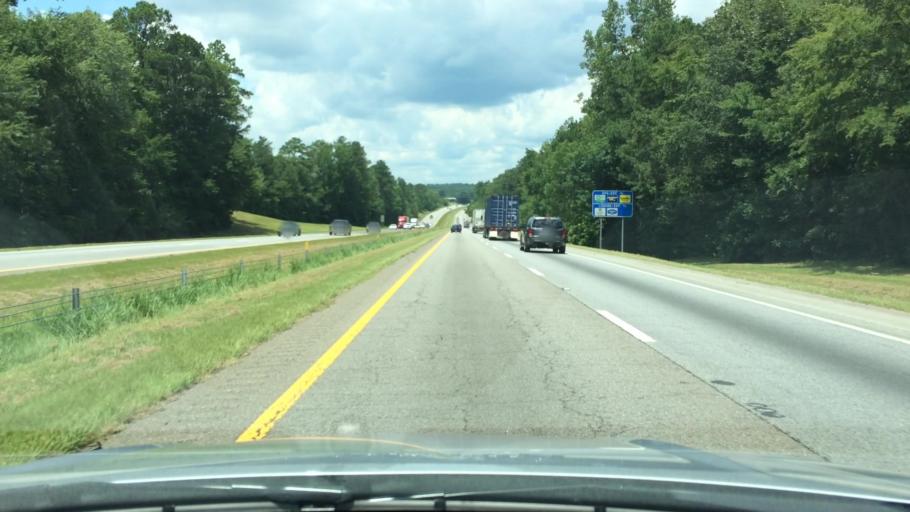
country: US
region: South Carolina
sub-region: Newberry County
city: Prosperity
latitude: 34.2858
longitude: -81.5337
